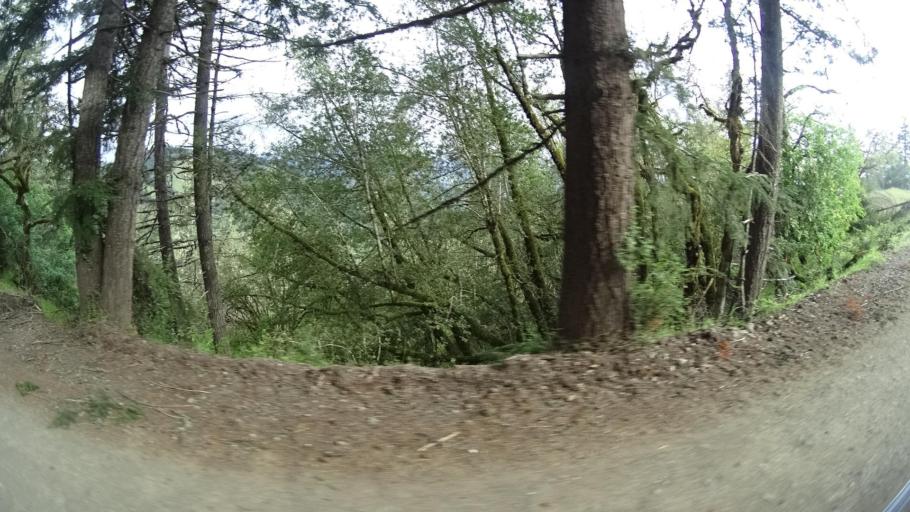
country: US
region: California
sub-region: Humboldt County
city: Redway
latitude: 40.2051
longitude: -123.7182
